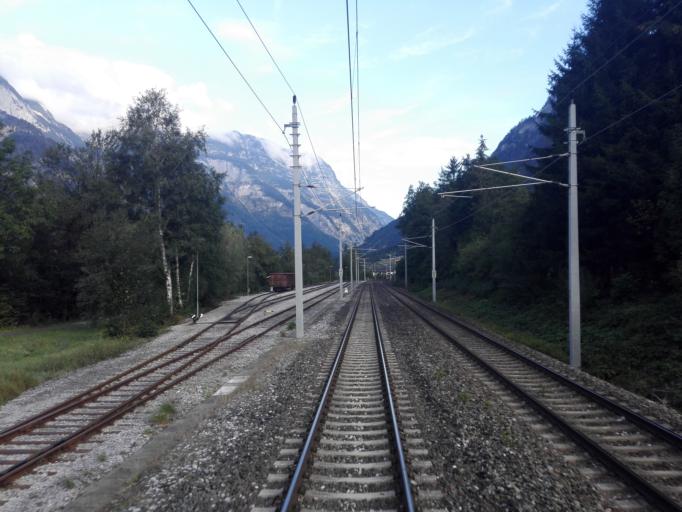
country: AT
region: Salzburg
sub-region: Politischer Bezirk Sankt Johann im Pongau
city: Werfen
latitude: 47.4961
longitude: 13.1785
